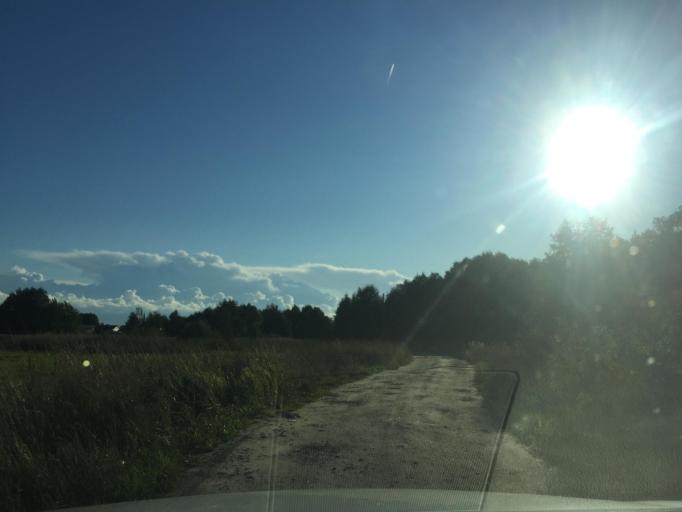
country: RU
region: Leningrad
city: Rozhdestveno
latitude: 59.3289
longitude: 29.9982
